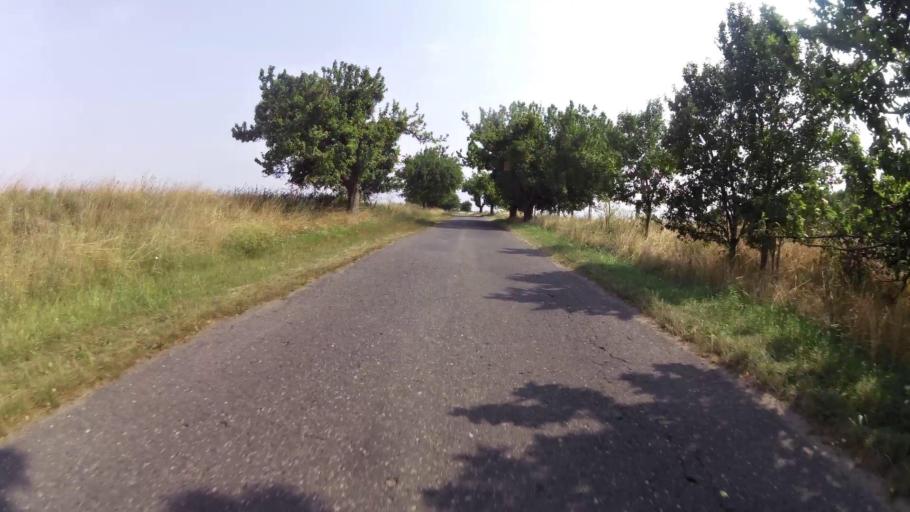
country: PL
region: West Pomeranian Voivodeship
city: Trzcinsko Zdroj
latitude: 52.8554
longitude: 14.6500
